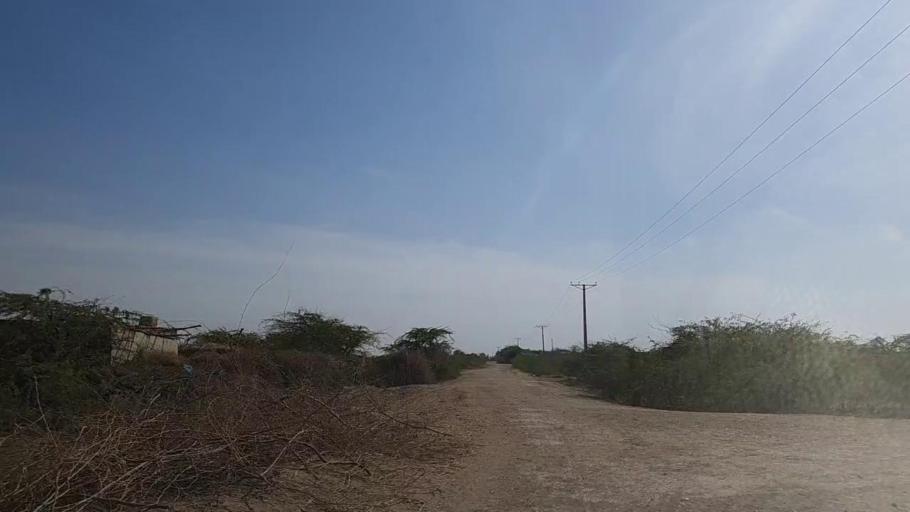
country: PK
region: Sindh
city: Samaro
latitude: 25.2075
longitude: 69.4362
